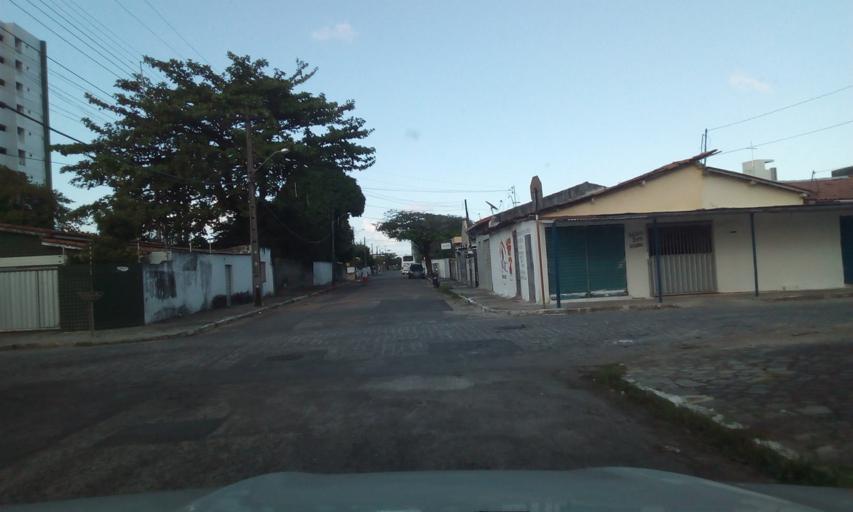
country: BR
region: Paraiba
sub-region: Joao Pessoa
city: Joao Pessoa
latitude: -7.1221
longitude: -34.8651
